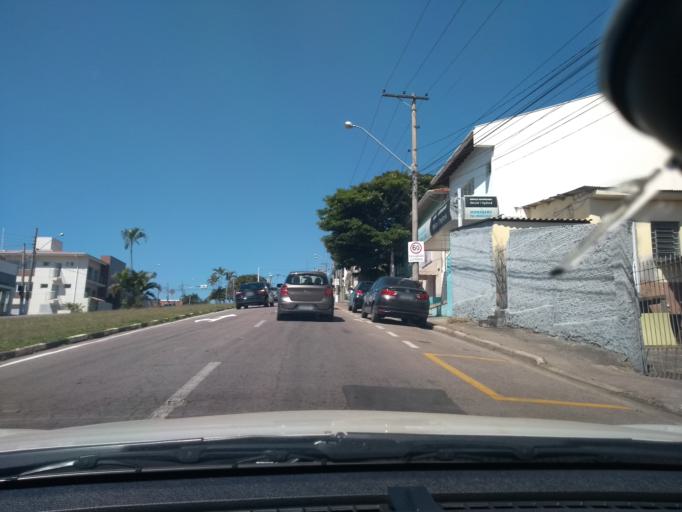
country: BR
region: Sao Paulo
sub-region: Vinhedo
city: Vinhedo
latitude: -23.0324
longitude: -46.9799
